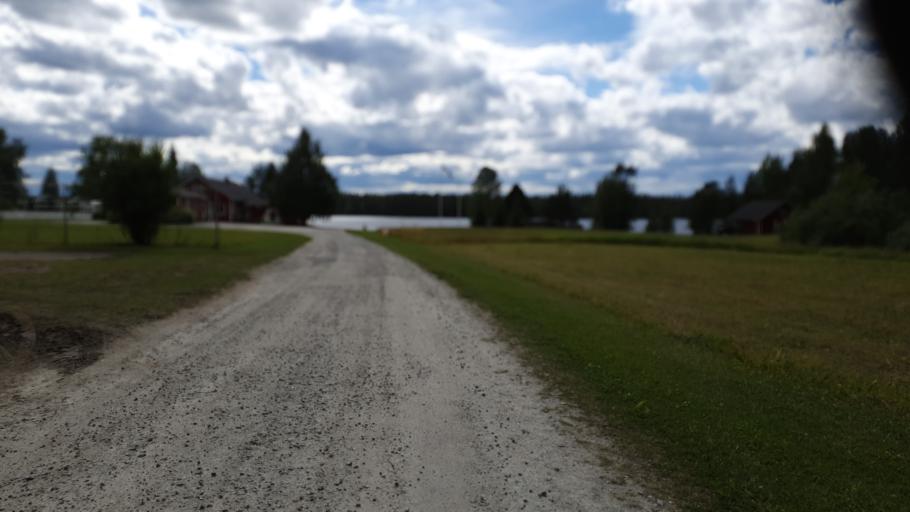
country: FI
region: Kainuu
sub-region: Kehys-Kainuu
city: Kuhmo
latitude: 64.3821
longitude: 29.7818
